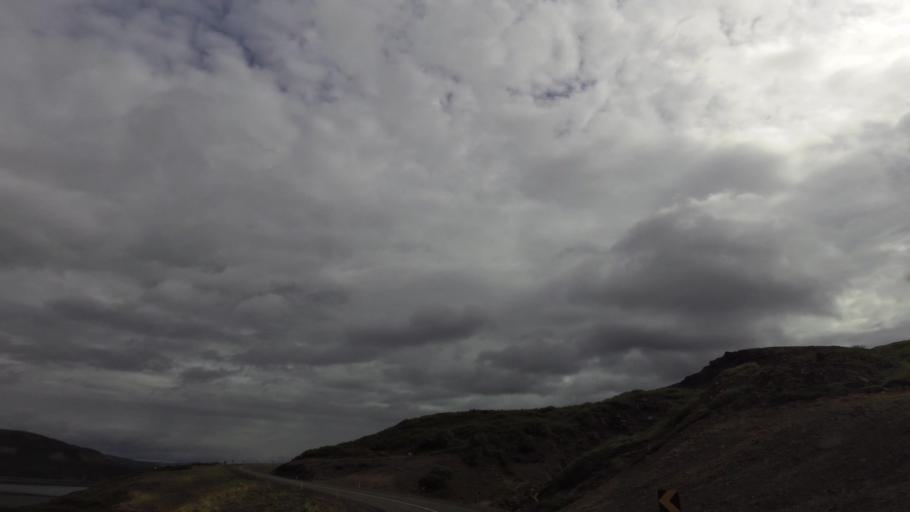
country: IS
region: West
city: Stykkisholmur
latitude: 65.5223
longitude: -22.1209
